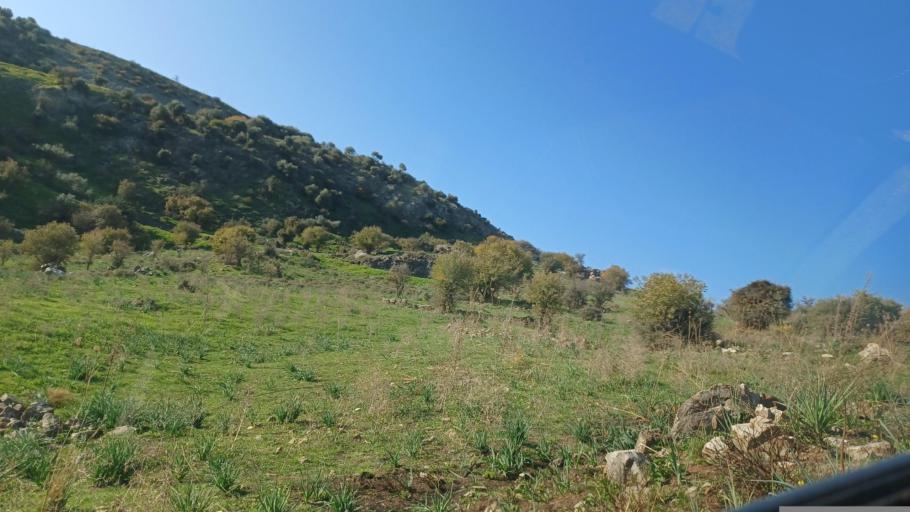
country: CY
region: Pafos
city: Mesogi
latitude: 34.7730
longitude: 32.5499
